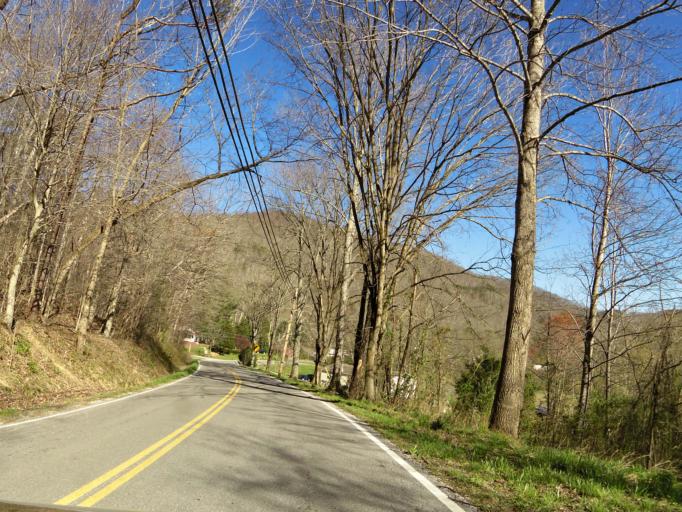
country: US
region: Tennessee
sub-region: Scott County
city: Huntsville
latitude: 36.3413
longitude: -84.3887
